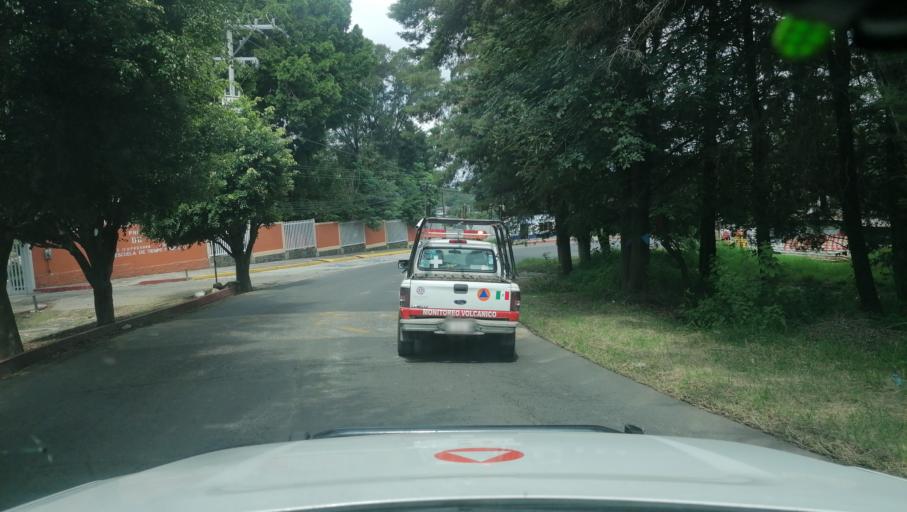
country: MX
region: Morelos
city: Ocuituco
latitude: 18.8783
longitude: -98.7821
